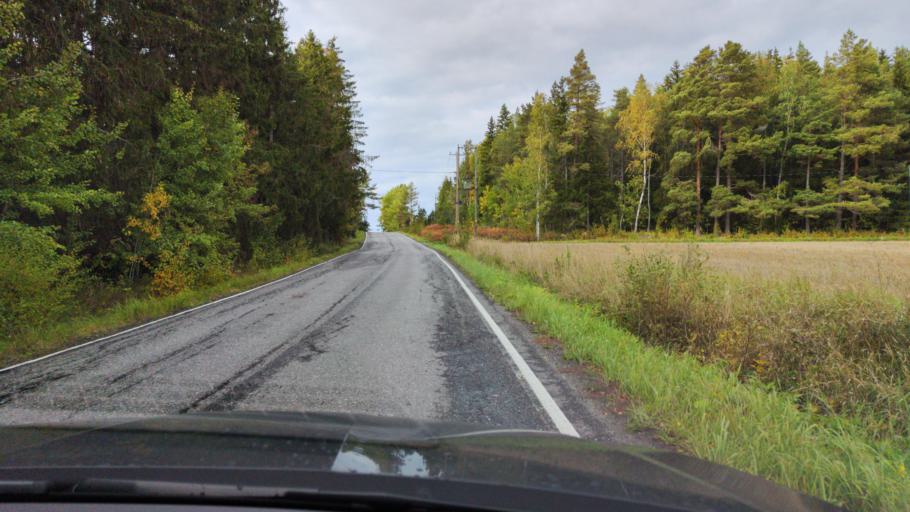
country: FI
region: Varsinais-Suomi
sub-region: Aboland-Turunmaa
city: Pargas
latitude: 60.3517
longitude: 22.1820
